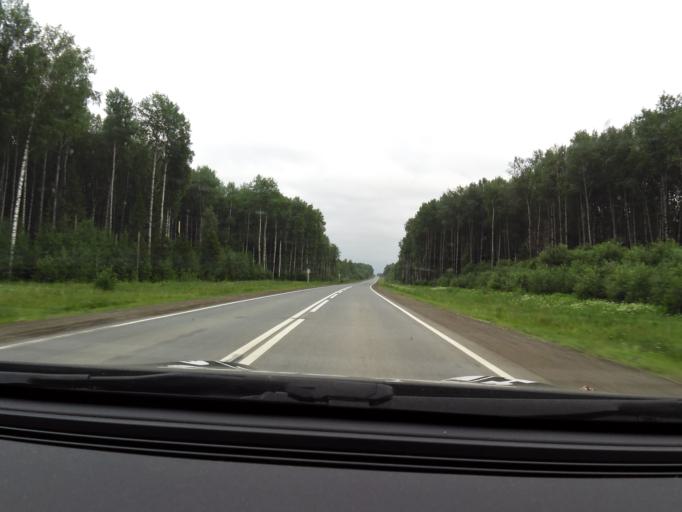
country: RU
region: Perm
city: Zyukayka
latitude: 58.3527
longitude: 54.7041
